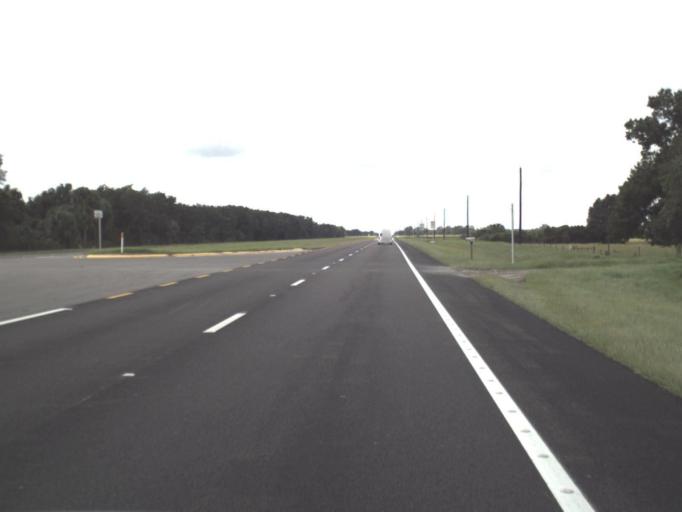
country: US
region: Florida
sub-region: Hardee County
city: Zolfo Springs
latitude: 27.4550
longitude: -81.7972
